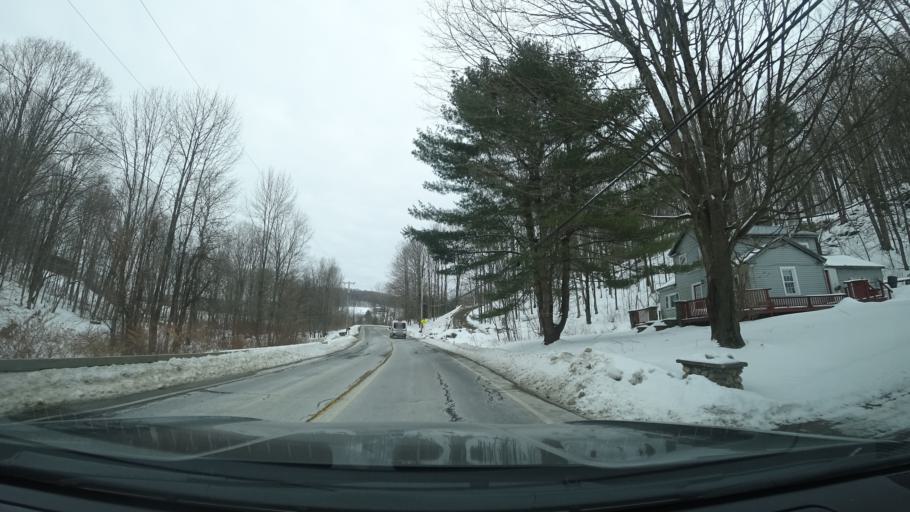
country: US
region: New York
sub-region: Washington County
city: Greenwich
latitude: 43.1849
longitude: -73.4920
